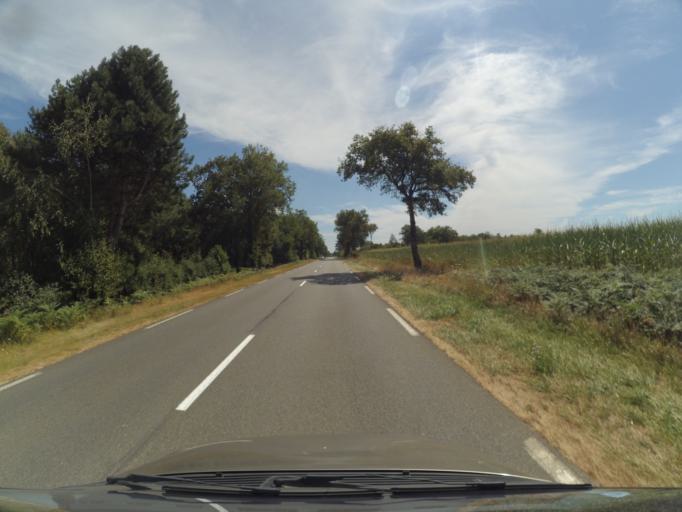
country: FR
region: Poitou-Charentes
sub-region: Departement de la Vienne
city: Availles-Limouzine
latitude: 46.0793
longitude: 0.5900
